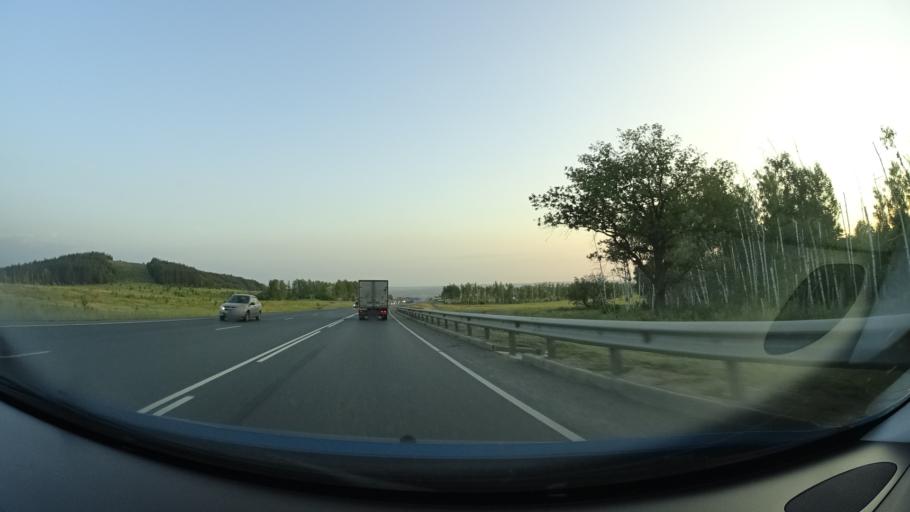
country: RU
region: Samara
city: Sernovodsk
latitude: 53.9144
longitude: 51.3017
